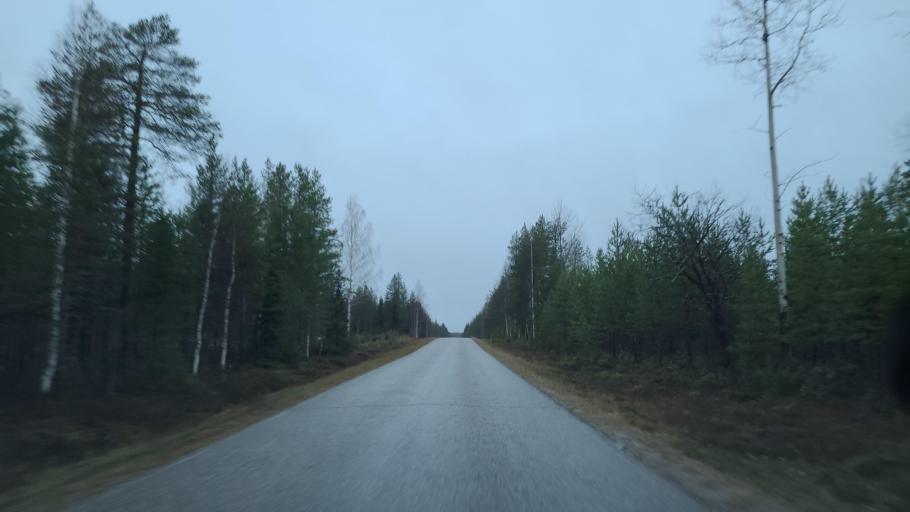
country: FI
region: Lapland
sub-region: Kemi-Tornio
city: Simo
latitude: 65.8909
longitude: 25.2163
